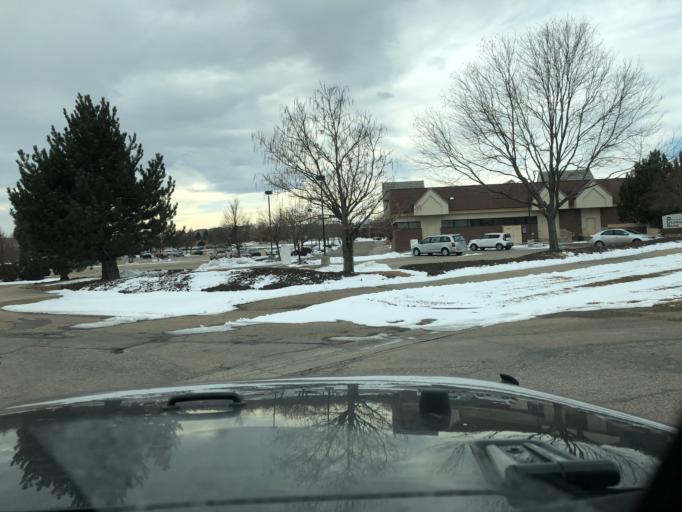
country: US
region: Colorado
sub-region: Boulder County
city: Longmont
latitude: 40.1886
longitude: -105.0724
